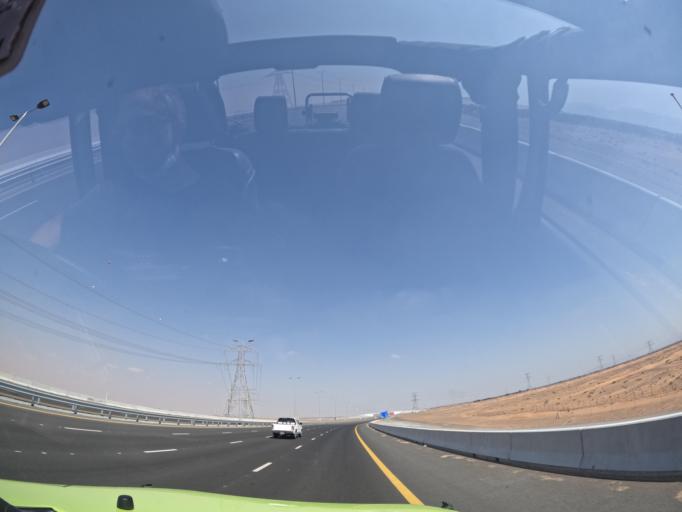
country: AE
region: Ash Shariqah
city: Adh Dhayd
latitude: 24.8044
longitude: 55.8009
